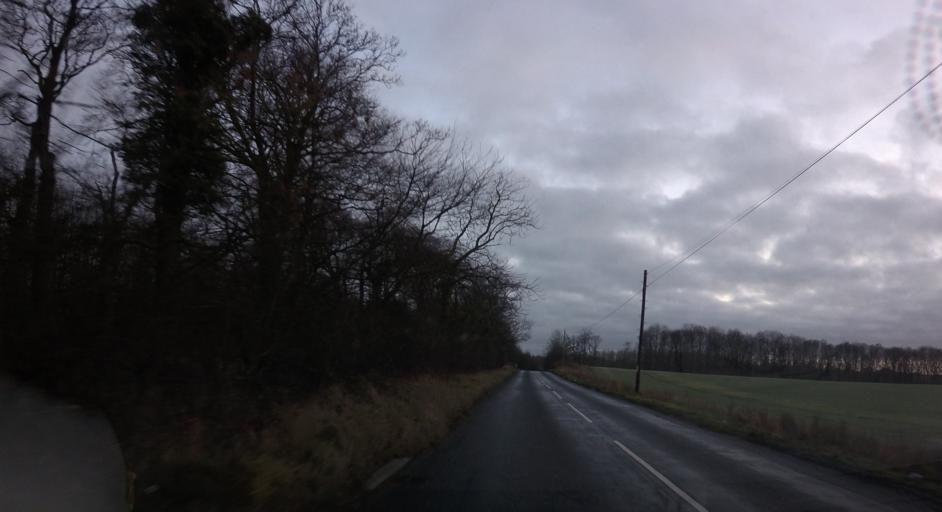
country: GB
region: Scotland
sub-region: Fife
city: Crossford
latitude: 56.0496
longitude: -3.4861
